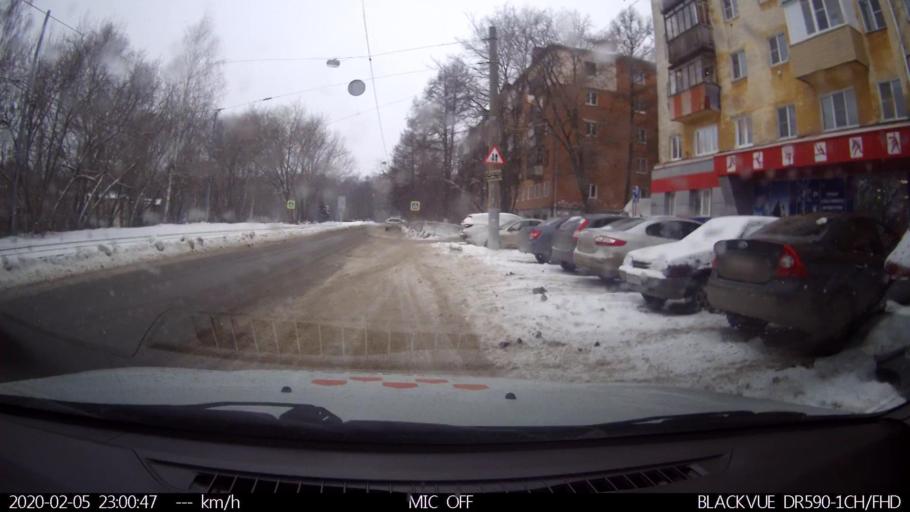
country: RU
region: Penza
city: Bogoslovka
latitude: 53.1714
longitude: 44.8776
